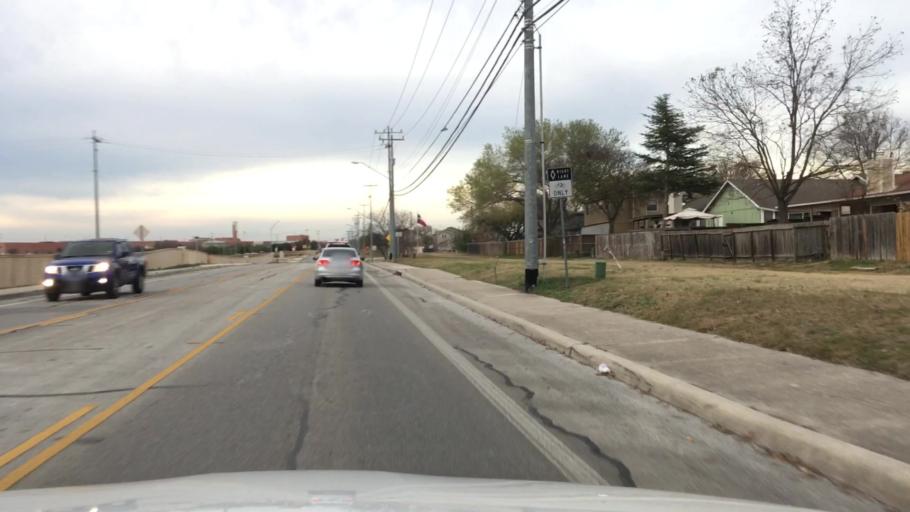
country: US
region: Texas
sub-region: Bexar County
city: Converse
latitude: 29.5392
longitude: -98.3170
